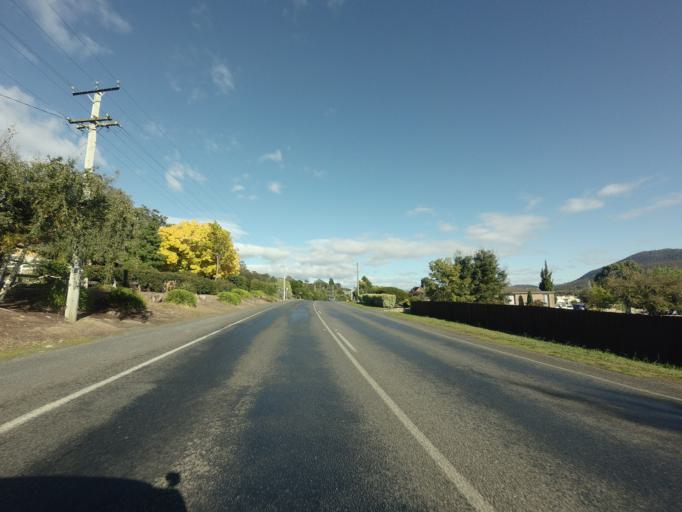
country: AU
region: Tasmania
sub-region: Derwent Valley
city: New Norfolk
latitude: -42.7843
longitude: 147.1014
